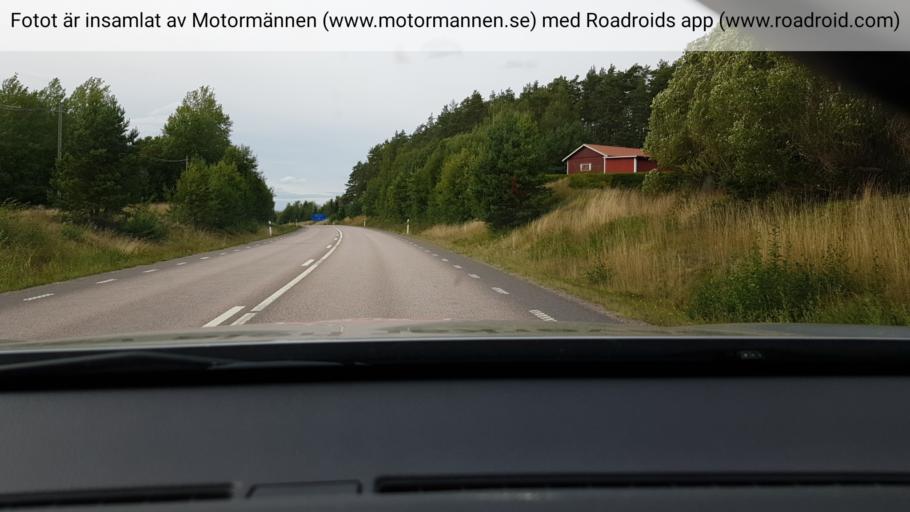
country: SE
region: Soedermanland
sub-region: Gnesta Kommun
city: Gnesta
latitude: 59.0455
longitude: 17.2887
